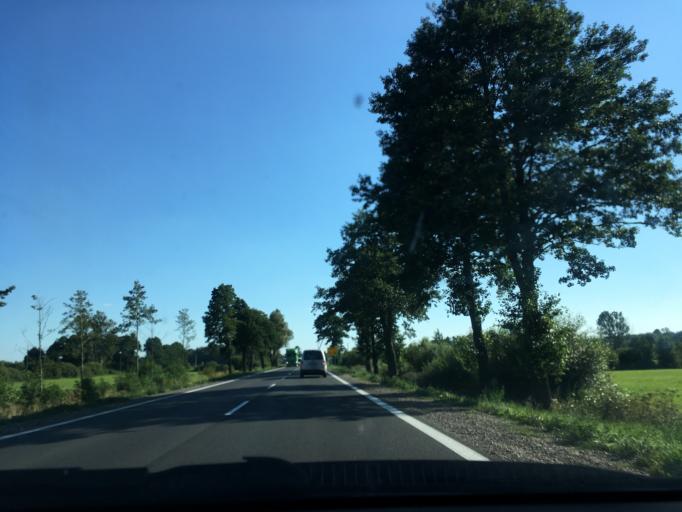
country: PL
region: Podlasie
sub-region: Powiat sokolski
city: Suchowola
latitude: 53.4599
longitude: 23.0884
